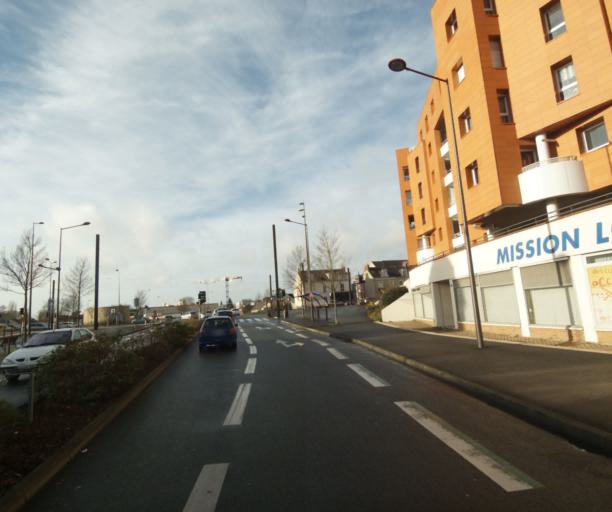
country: FR
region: Pays de la Loire
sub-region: Departement de la Sarthe
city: Le Mans
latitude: 47.9865
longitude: 0.2100
